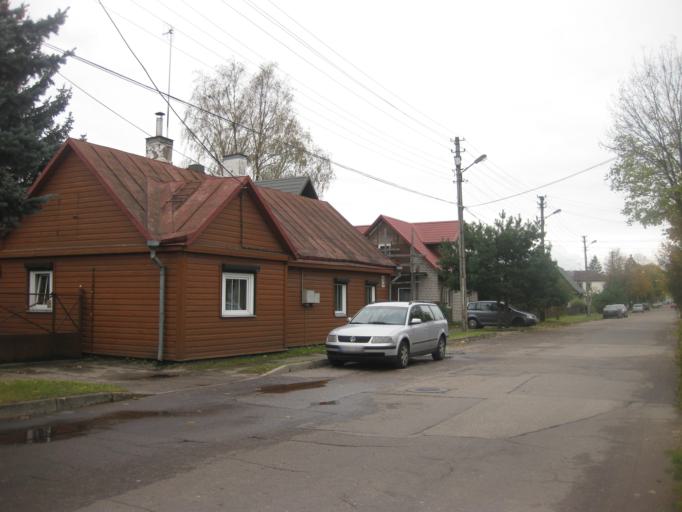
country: LT
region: Kauno apskritis
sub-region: Kaunas
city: Eiguliai
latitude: 54.9101
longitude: 23.9245
